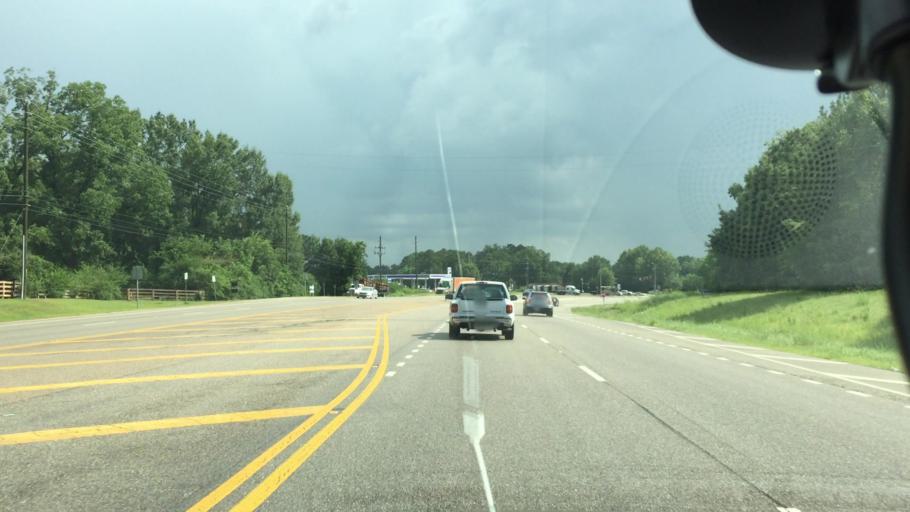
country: US
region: Alabama
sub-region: Montgomery County
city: Pike Road
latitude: 32.3003
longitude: -86.1959
